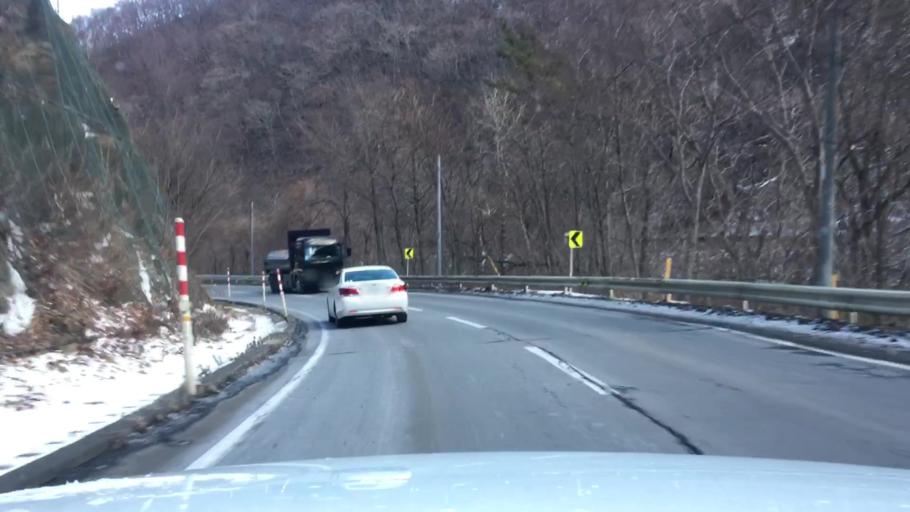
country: JP
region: Iwate
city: Tono
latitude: 39.6181
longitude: 141.5044
